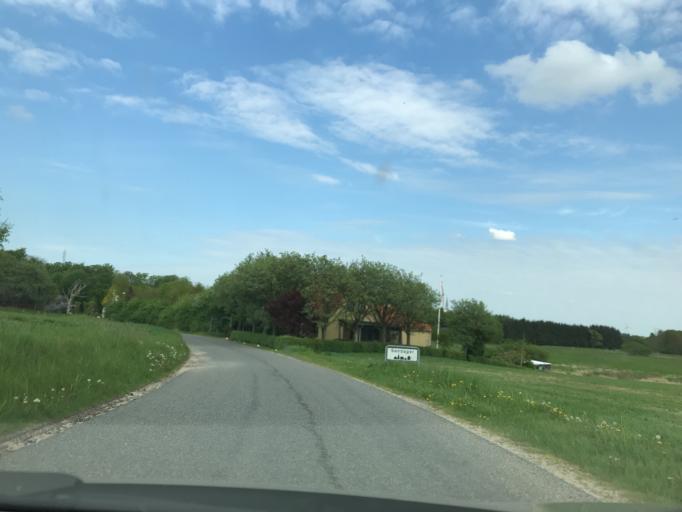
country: DK
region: South Denmark
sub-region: Assens Kommune
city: Assens
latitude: 55.3259
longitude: 9.9196
